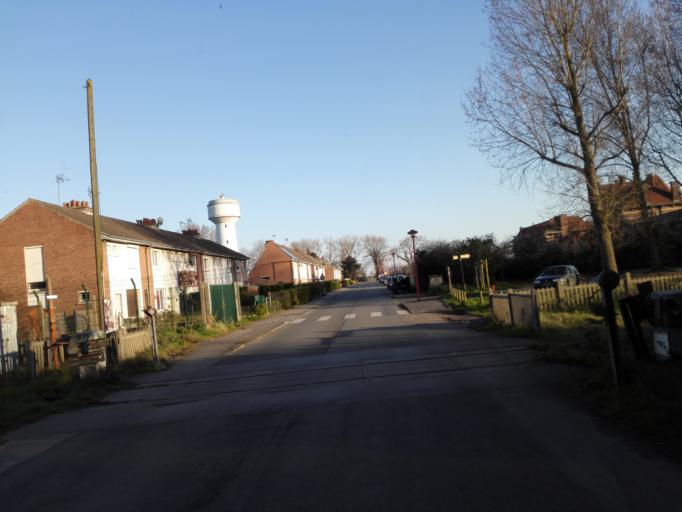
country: FR
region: Nord-Pas-de-Calais
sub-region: Departement du Nord
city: Zuydcoote
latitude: 51.0631
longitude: 2.4820
